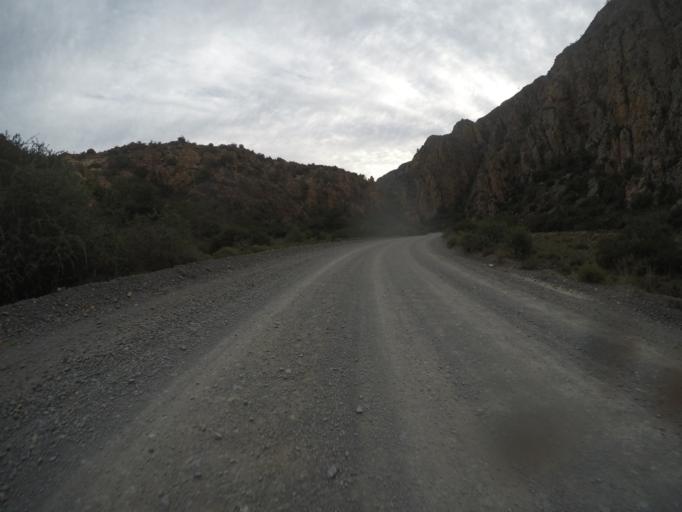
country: ZA
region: Eastern Cape
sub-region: Cacadu District Municipality
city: Willowmore
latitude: -33.5192
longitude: 23.6766
